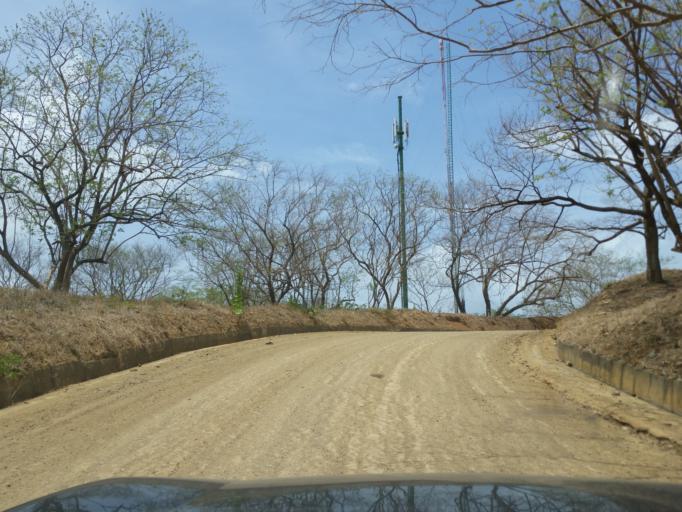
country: NI
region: Rivas
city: Tola
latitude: 11.4395
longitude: -86.0838
